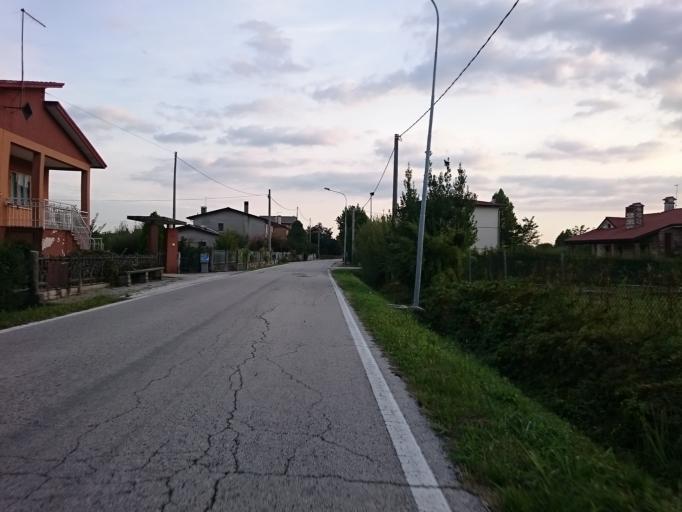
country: IT
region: Veneto
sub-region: Provincia di Vicenza
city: Grisignano di Zocco
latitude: 45.4903
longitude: 11.7093
